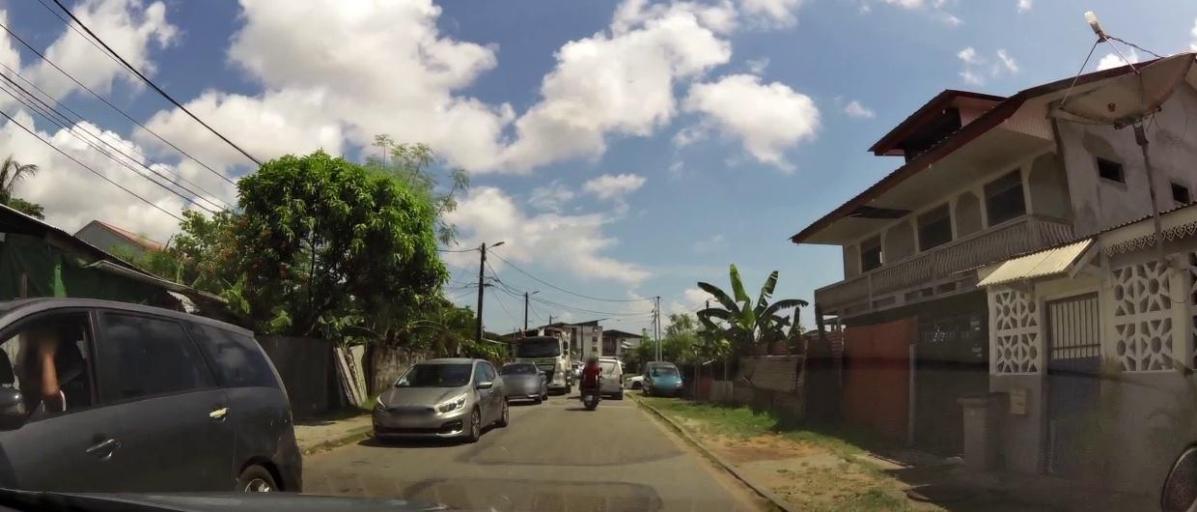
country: GF
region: Guyane
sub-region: Guyane
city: Cayenne
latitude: 4.9223
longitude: -52.3195
